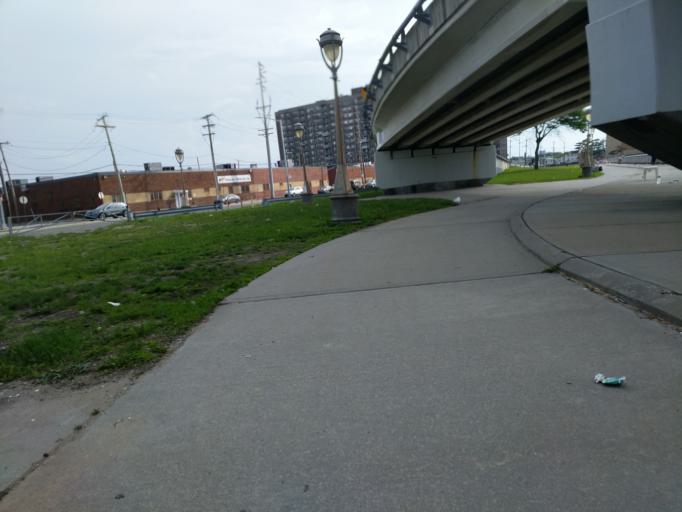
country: US
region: New York
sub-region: Nassau County
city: Inwood
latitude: 40.5879
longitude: -73.8192
